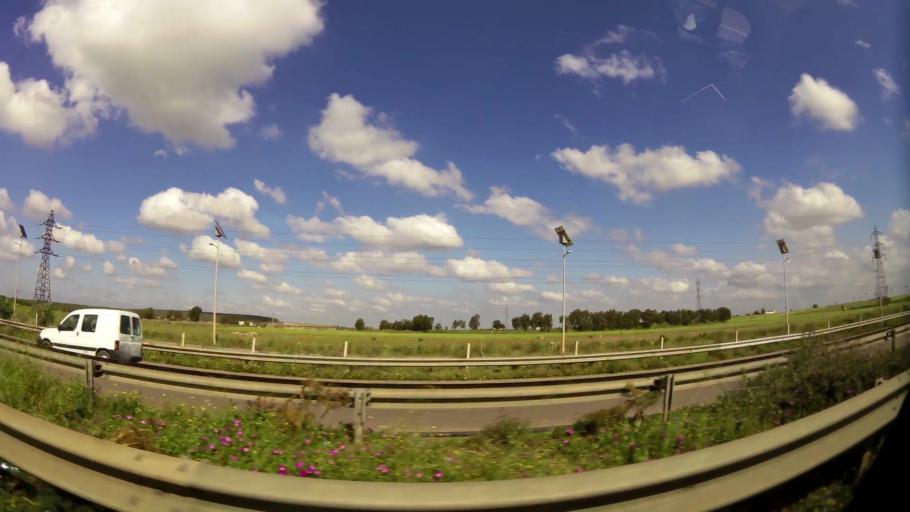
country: MA
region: Grand Casablanca
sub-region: Nouaceur
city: Bouskoura
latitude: 33.4269
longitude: -7.6275
